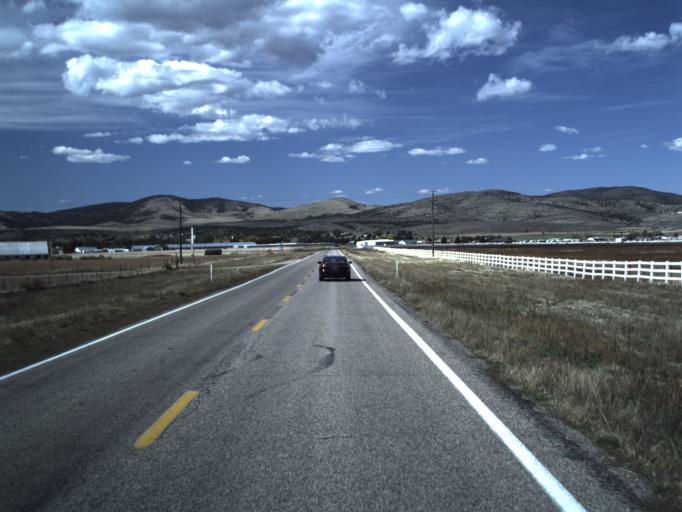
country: US
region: Utah
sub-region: Washington County
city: Enterprise
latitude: 37.5679
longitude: -113.6970
